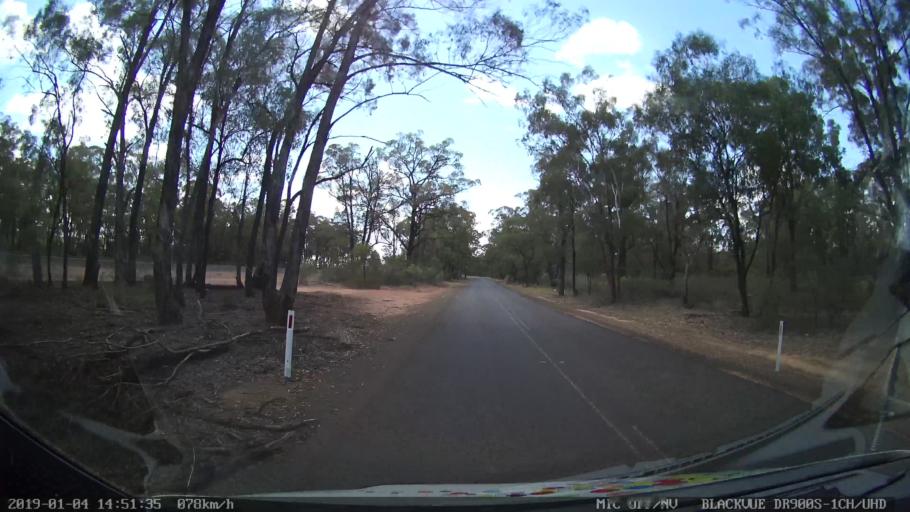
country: AU
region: New South Wales
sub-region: Dubbo Municipality
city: Dubbo
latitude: -32.0255
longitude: 148.6515
